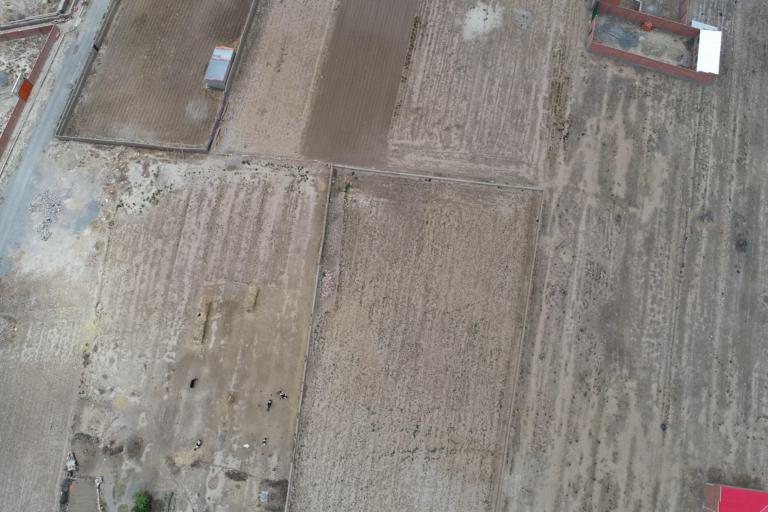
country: BO
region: La Paz
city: Achacachi
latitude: -16.0447
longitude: -68.6930
